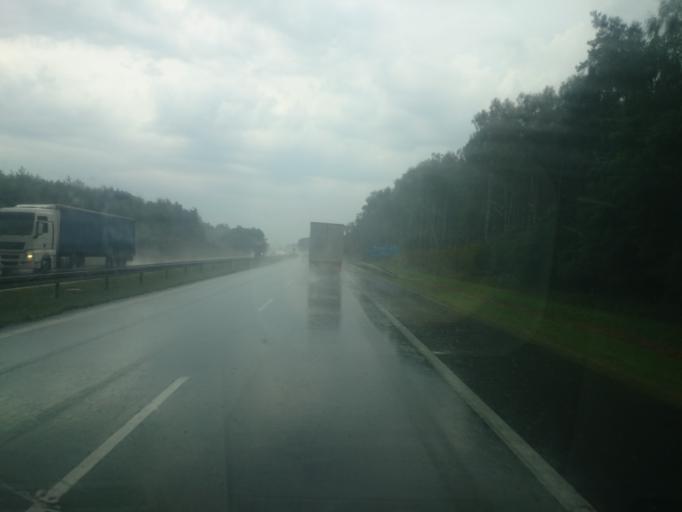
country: PL
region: Opole Voivodeship
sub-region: Powiat strzelecki
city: Strzelce Opolskie
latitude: 50.4540
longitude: 18.2971
